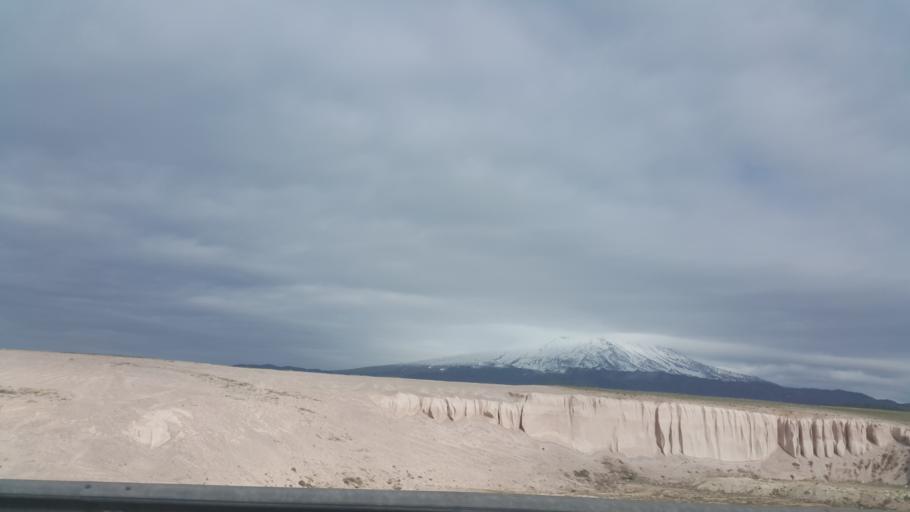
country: TR
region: Aksaray
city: Taspinar
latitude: 38.1632
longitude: 34.0365
